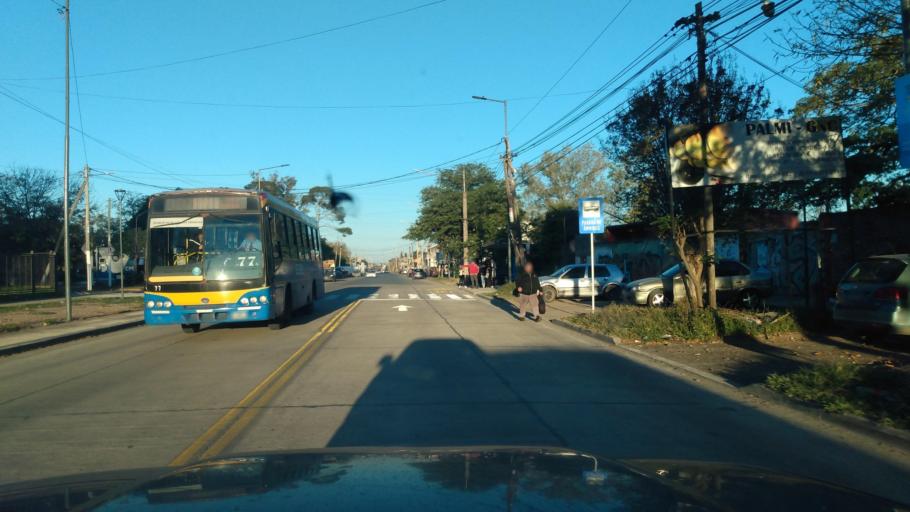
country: AR
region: Buenos Aires
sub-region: Partido de Merlo
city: Merlo
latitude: -34.6536
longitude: -58.7738
